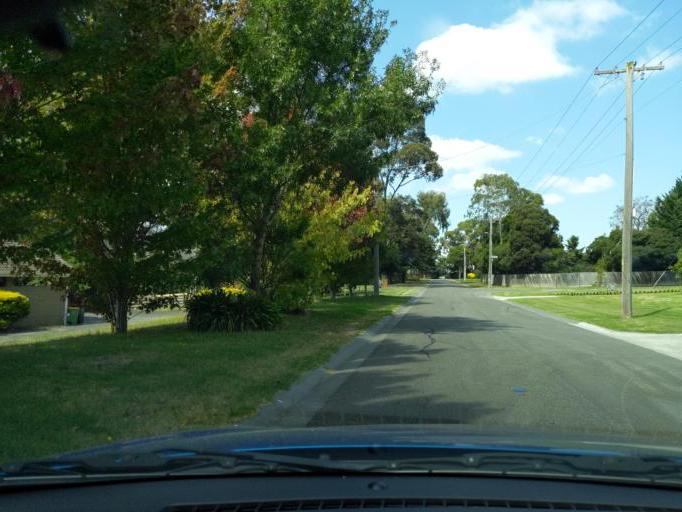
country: AU
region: Victoria
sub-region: Knox
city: Rowville
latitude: -37.9238
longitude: 145.2509
